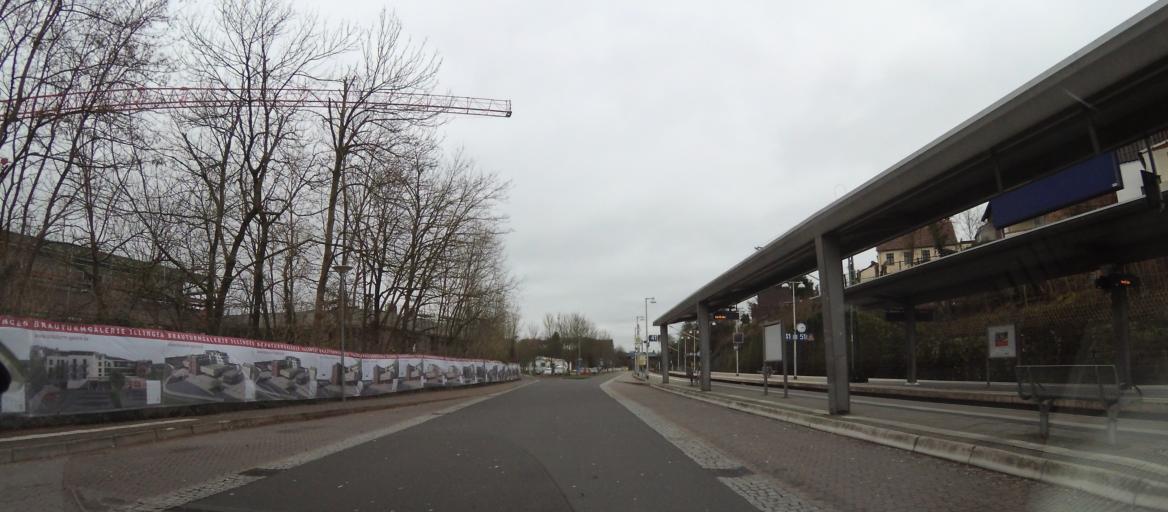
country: DE
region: Saarland
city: Illingen
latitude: 49.3767
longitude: 7.0492
